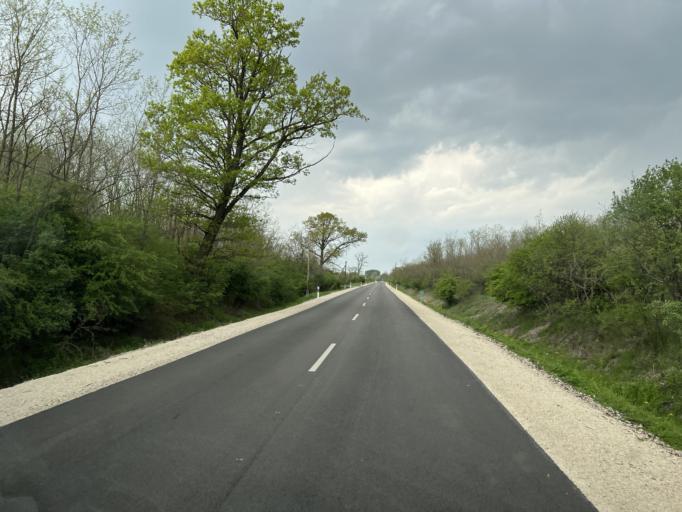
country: HU
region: Pest
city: Csemo
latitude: 47.0605
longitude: 19.7114
